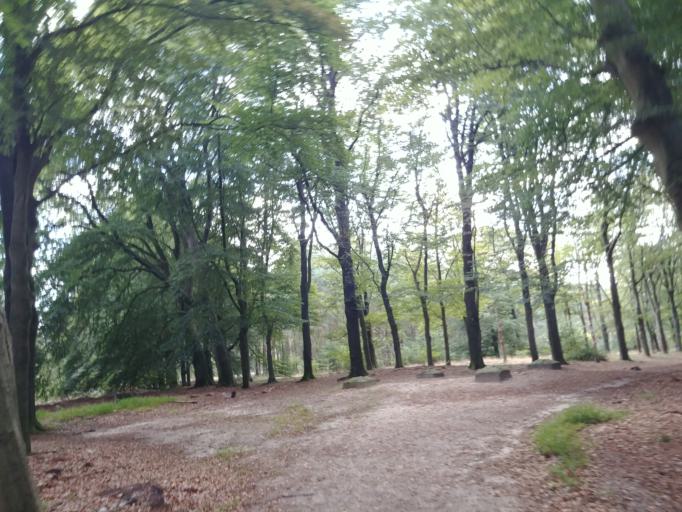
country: NL
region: Utrecht
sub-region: Gemeente Utrechtse Heuvelrug
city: Doorn
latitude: 52.0380
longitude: 5.3637
